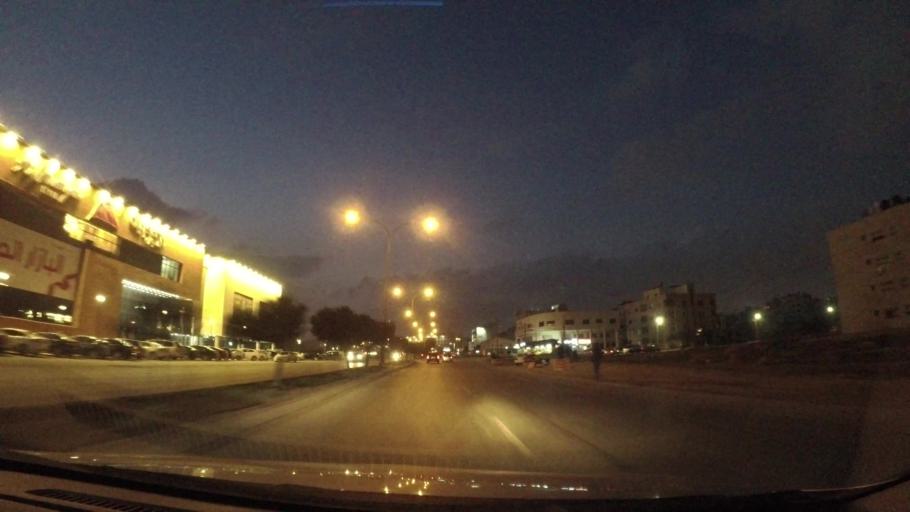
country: JO
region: Amman
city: Al Bunayyat ash Shamaliyah
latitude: 31.9042
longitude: 35.8880
